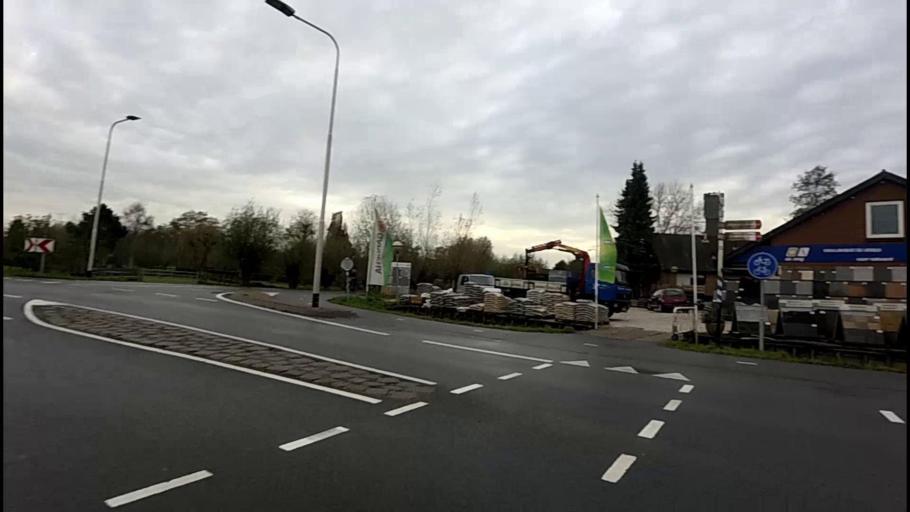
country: NL
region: South Holland
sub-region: Gemeente Alblasserdam
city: Alblasserdam
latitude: 51.8977
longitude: 4.6406
